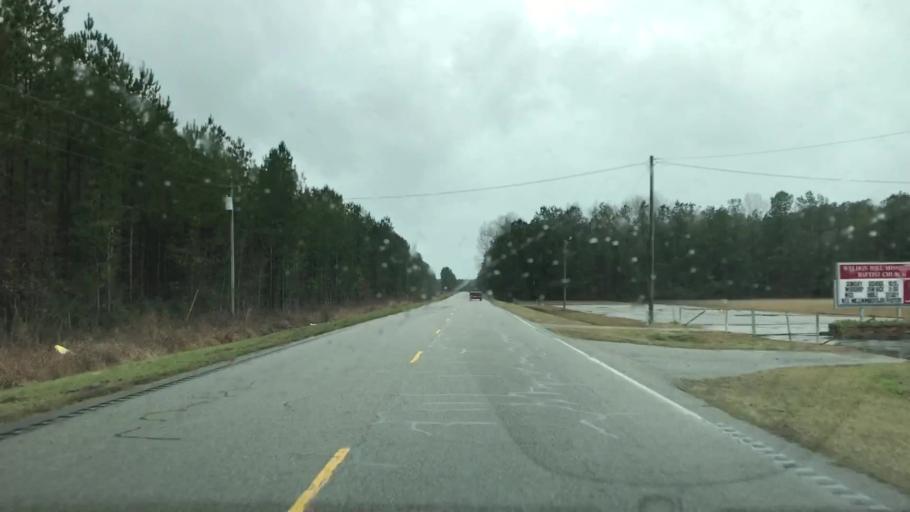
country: US
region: South Carolina
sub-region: Williamsburg County
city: Andrews
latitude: 33.5418
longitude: -79.4772
